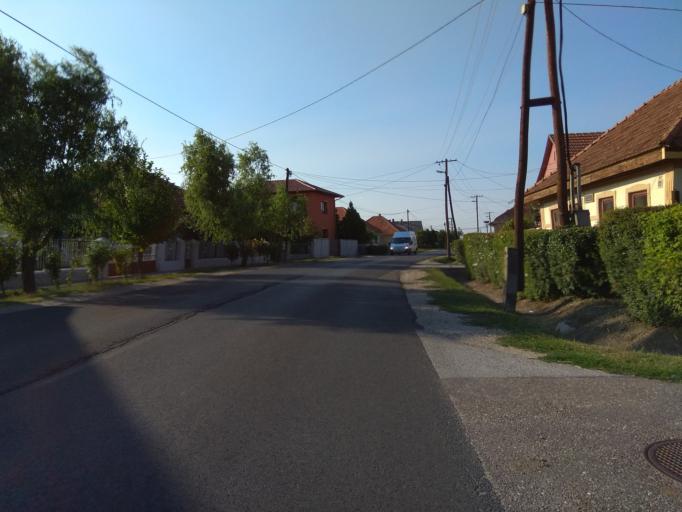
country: HU
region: Borsod-Abauj-Zemplen
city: Onod
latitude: 48.0072
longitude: 20.9129
